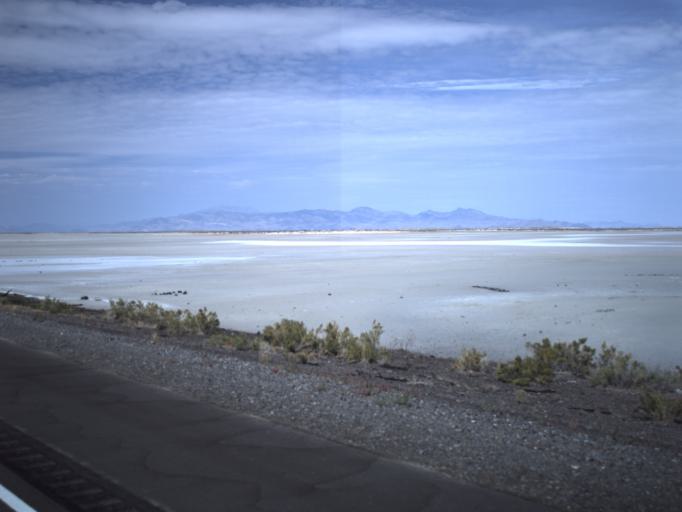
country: US
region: Utah
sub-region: Tooele County
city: Wendover
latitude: 40.7305
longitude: -113.4438
